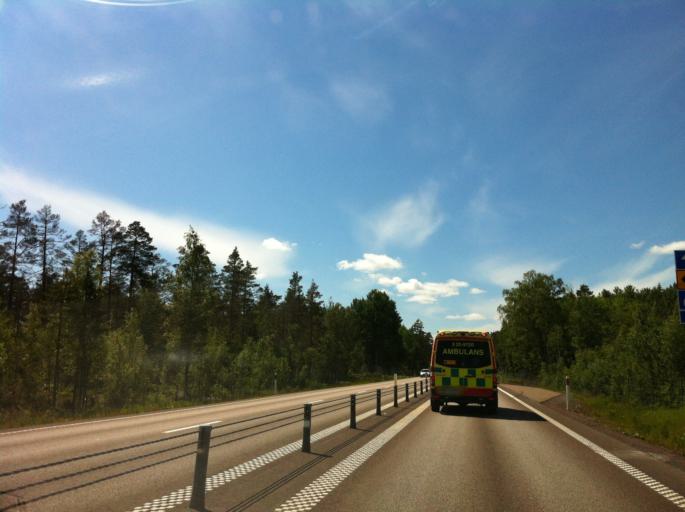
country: SE
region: Vaestra Goetaland
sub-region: Melleruds Kommun
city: Mellerud
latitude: 58.8406
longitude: 12.5440
